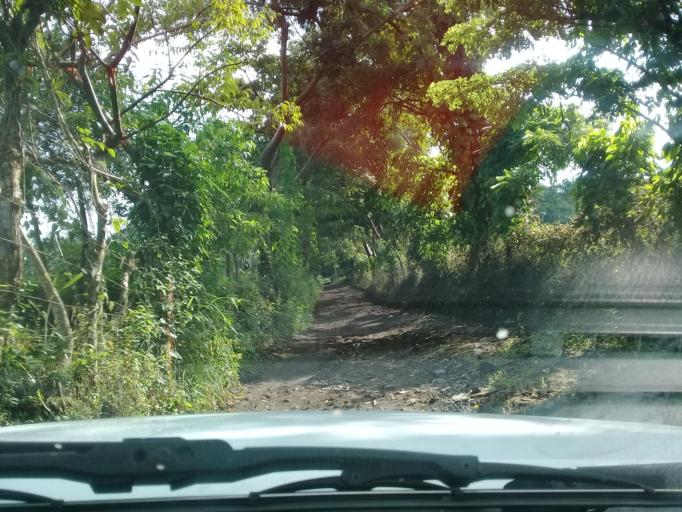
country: MX
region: Veracruz
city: Catemaco
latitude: 18.4359
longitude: -95.1309
